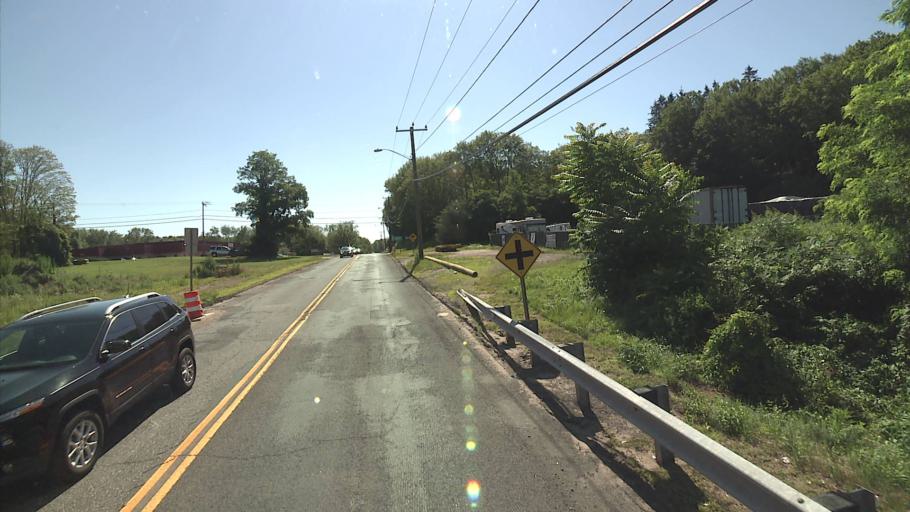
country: US
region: Connecticut
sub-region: Middlesex County
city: East Hampton
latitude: 41.5640
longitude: -72.5394
